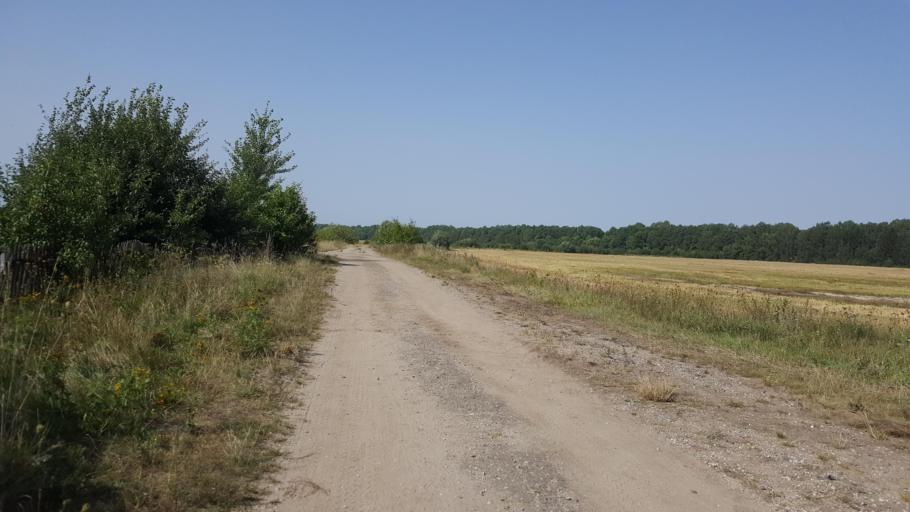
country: BY
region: Brest
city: Pruzhany
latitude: 52.4919
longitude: 24.6073
